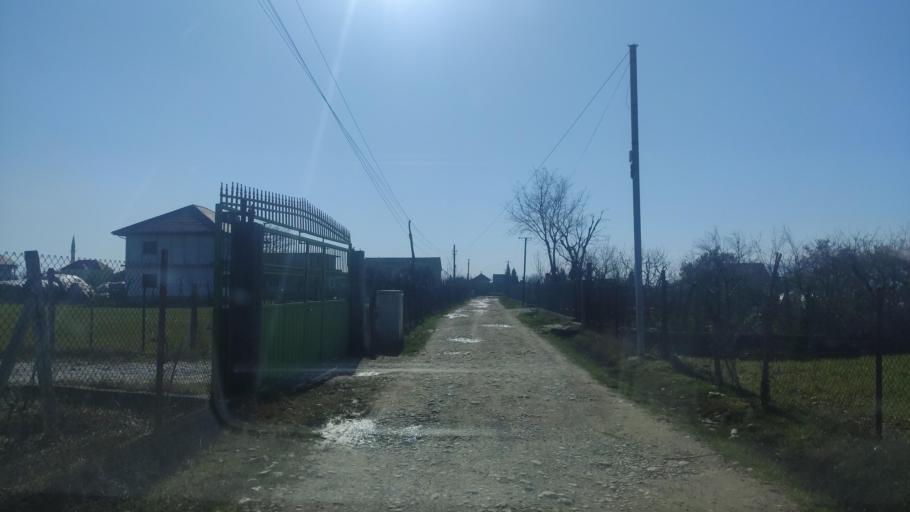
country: AL
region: Shkoder
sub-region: Rrethi i Malesia e Madhe
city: Grude-Fushe
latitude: 42.1636
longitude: 19.4573
